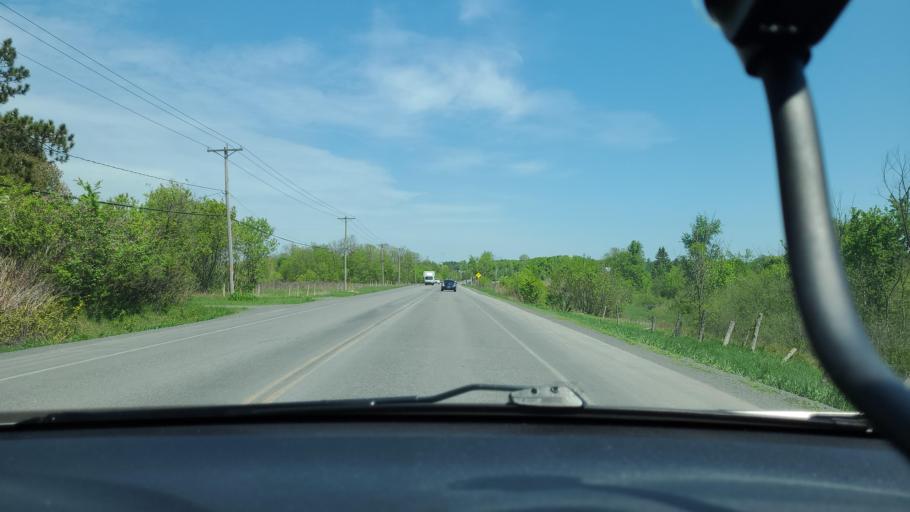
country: CA
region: Quebec
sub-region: Laurentides
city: Saint-Colomban
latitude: 45.6685
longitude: -74.2180
